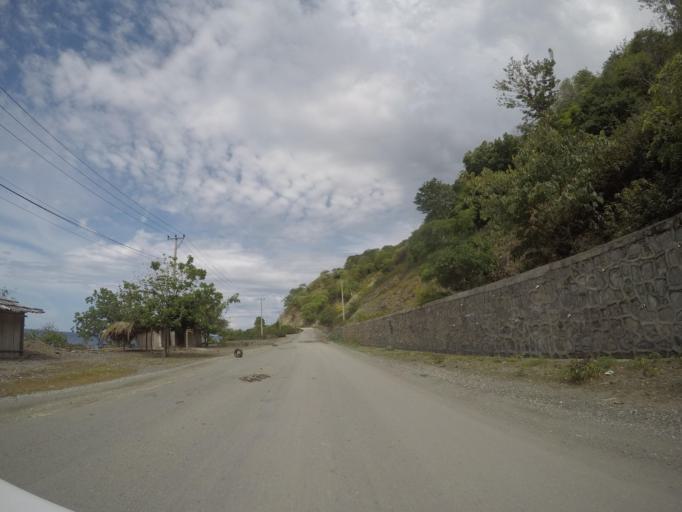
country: TL
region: Liquica
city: Maubara
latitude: -8.6256
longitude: 125.1638
